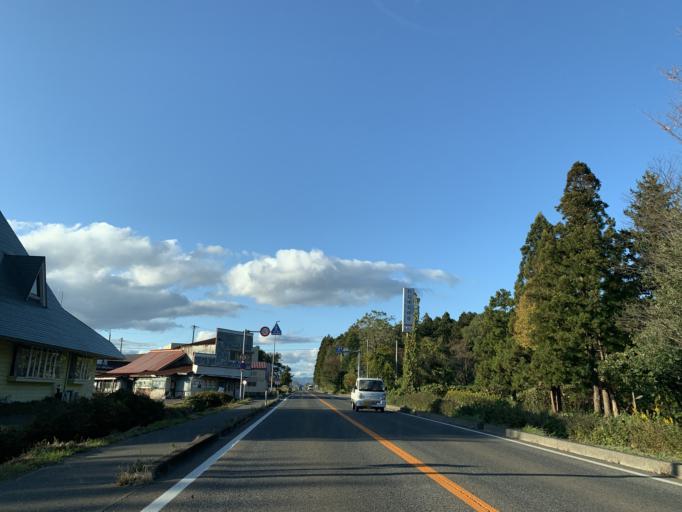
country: JP
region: Iwate
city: Kitakami
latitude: 39.2103
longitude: 141.1059
